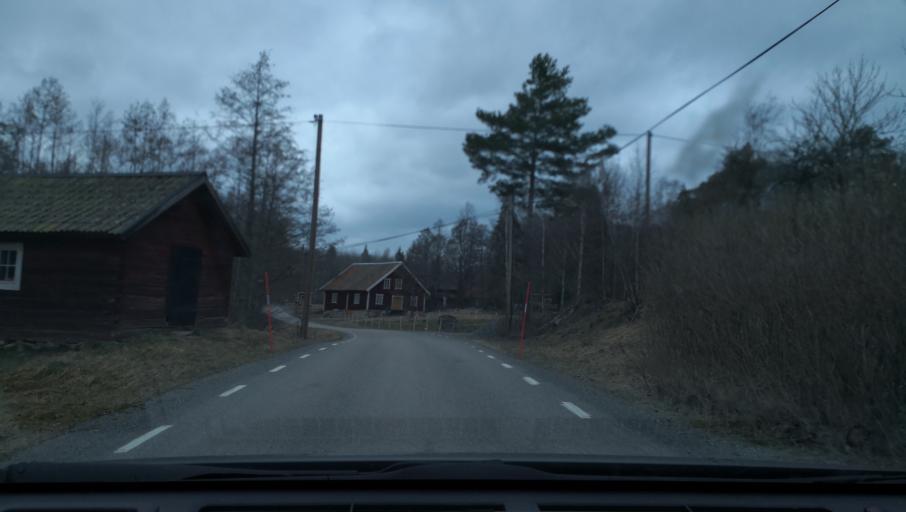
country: SE
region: Vaestmanland
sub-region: Kopings Kommun
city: Kolsva
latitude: 59.5675
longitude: 15.7314
